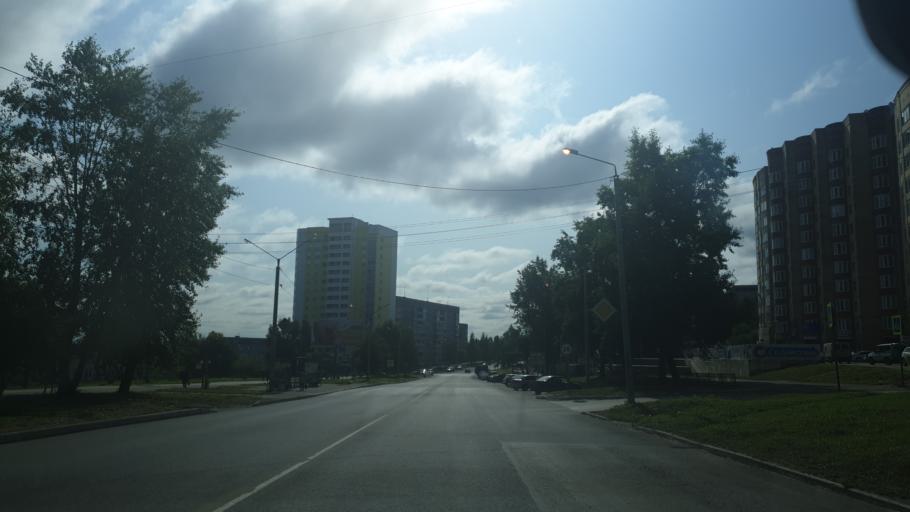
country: RU
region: Komi Republic
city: Ezhva
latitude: 61.7866
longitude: 50.7551
